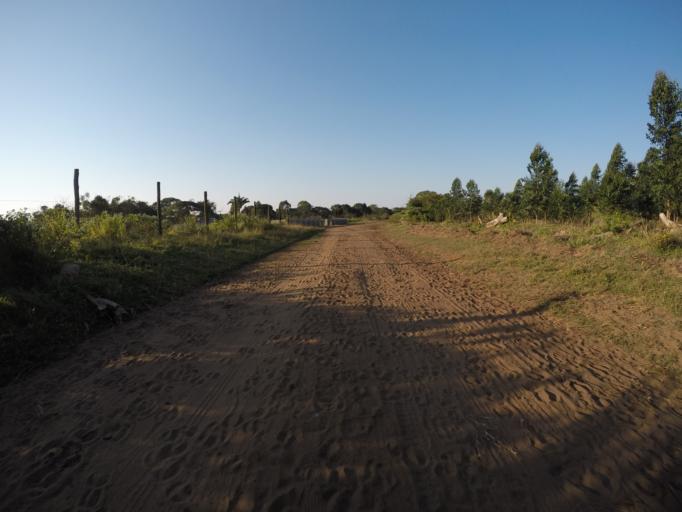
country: ZA
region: KwaZulu-Natal
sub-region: uThungulu District Municipality
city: KwaMbonambi
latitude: -28.6923
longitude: 32.2011
